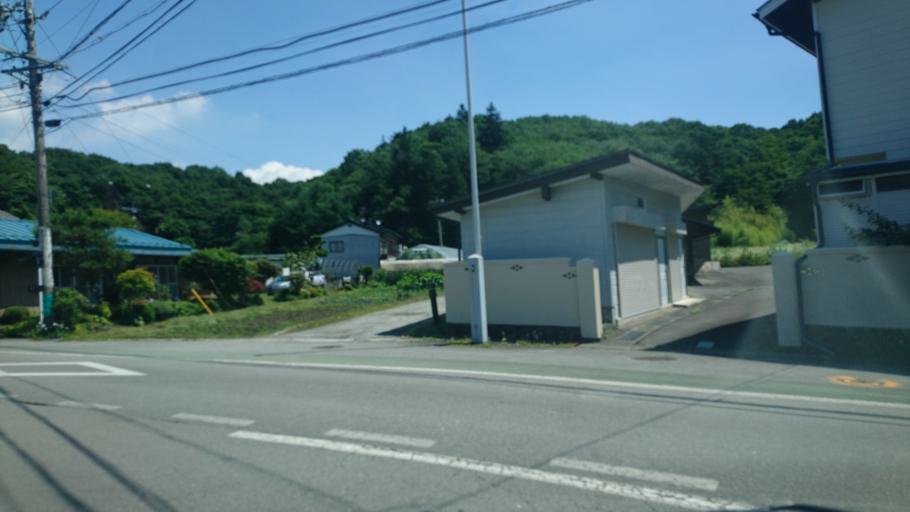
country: JP
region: Nagano
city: Saku
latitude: 36.3140
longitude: 138.5928
